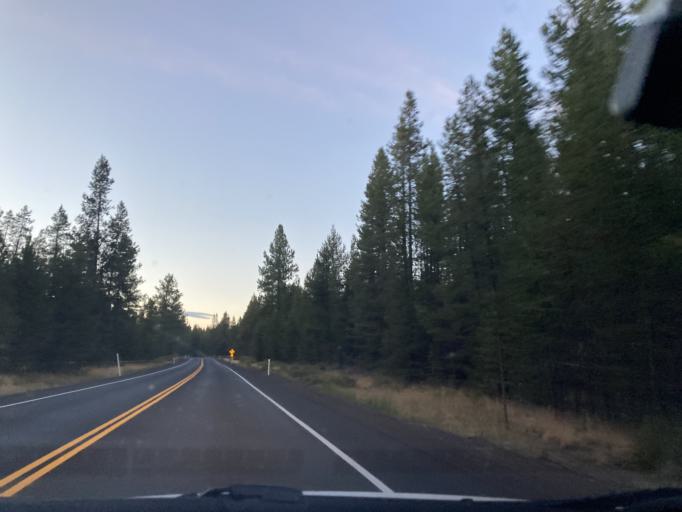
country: US
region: Oregon
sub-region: Deschutes County
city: Three Rivers
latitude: 43.8297
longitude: -121.4413
